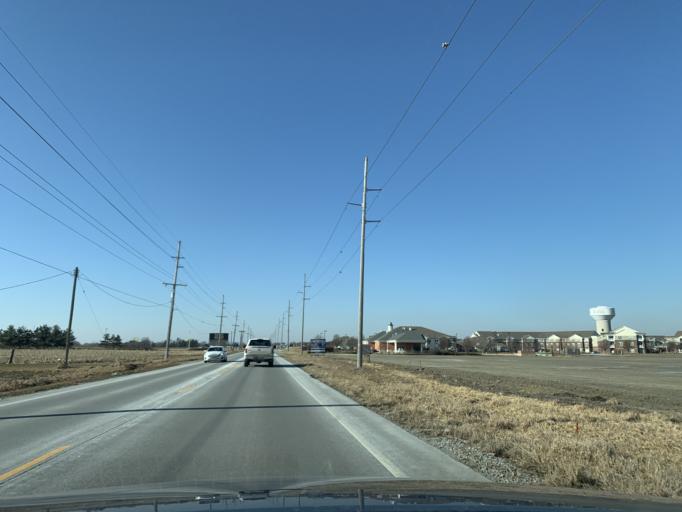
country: US
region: Indiana
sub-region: Lake County
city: Saint John
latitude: 41.4210
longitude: -87.4383
